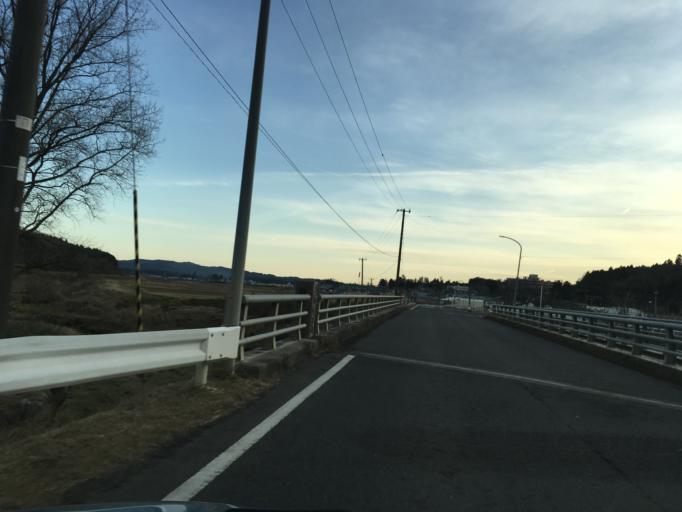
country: JP
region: Miyagi
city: Kogota
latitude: 38.6606
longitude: 141.0736
